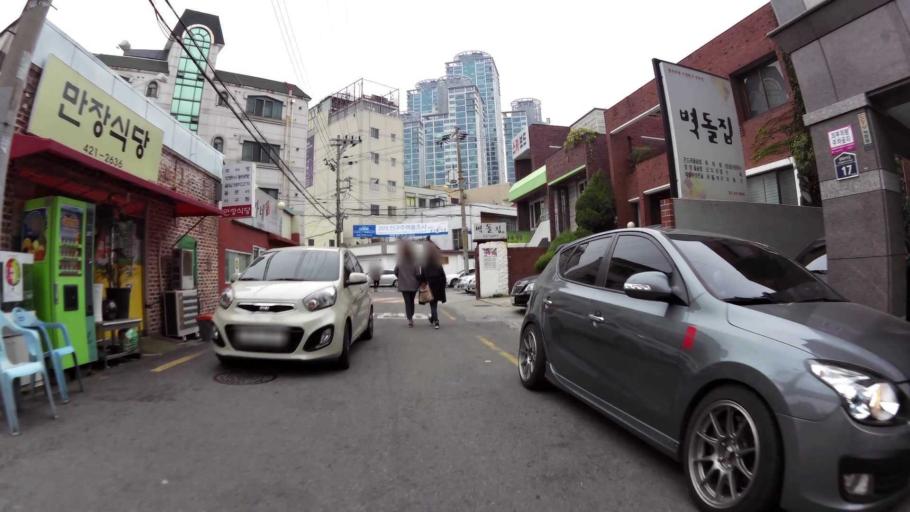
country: KR
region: Daegu
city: Daegu
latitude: 35.8610
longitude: 128.6048
